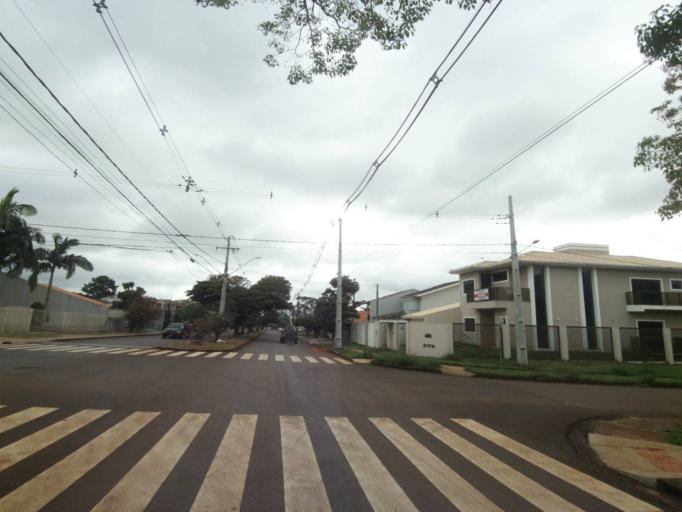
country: BR
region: Parana
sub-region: Campo Mourao
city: Campo Mourao
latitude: -24.0412
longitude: -52.3666
